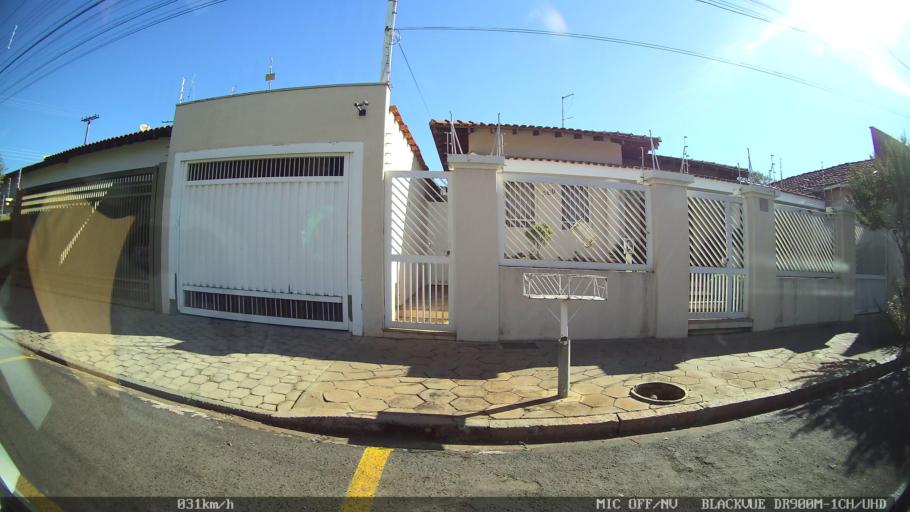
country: BR
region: Sao Paulo
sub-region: Olimpia
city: Olimpia
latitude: -20.7404
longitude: -48.9170
